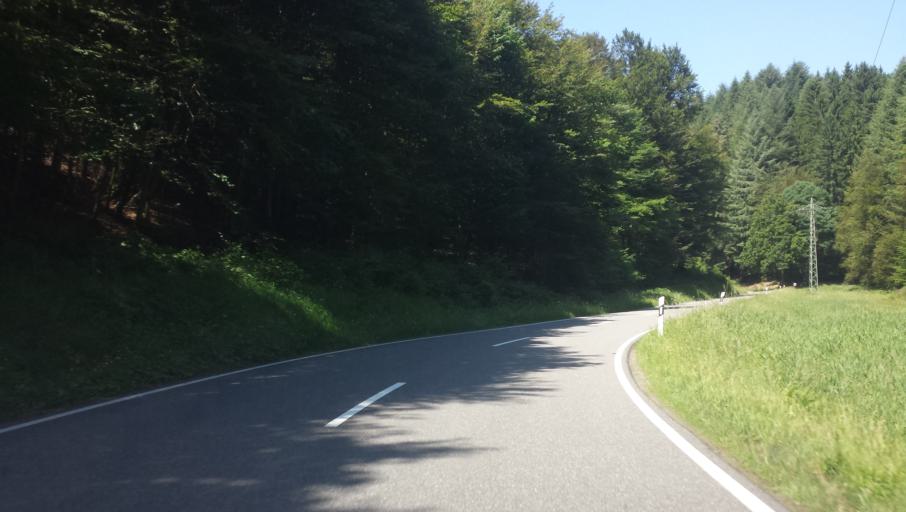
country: DE
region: Rheinland-Pfalz
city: Waldleiningen
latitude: 49.3495
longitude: 7.8556
